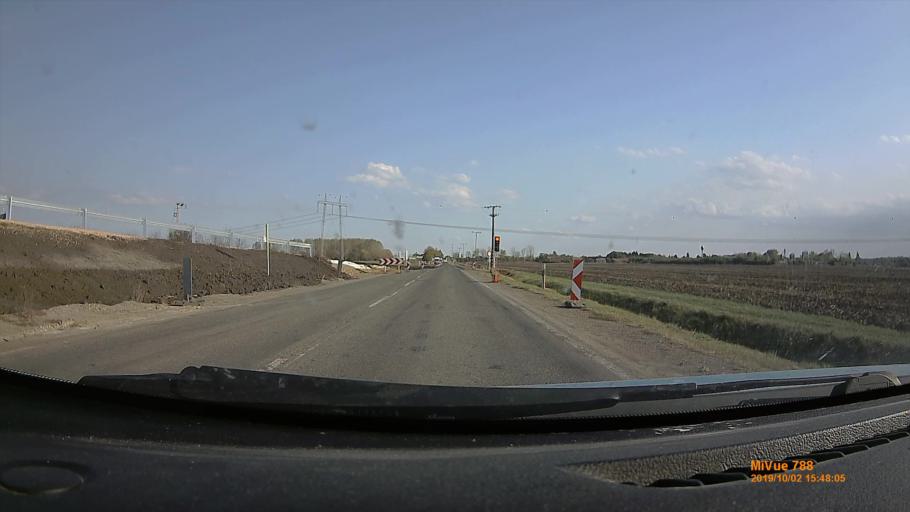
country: HU
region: Heves
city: Kerecsend
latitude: 47.7740
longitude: 20.3764
